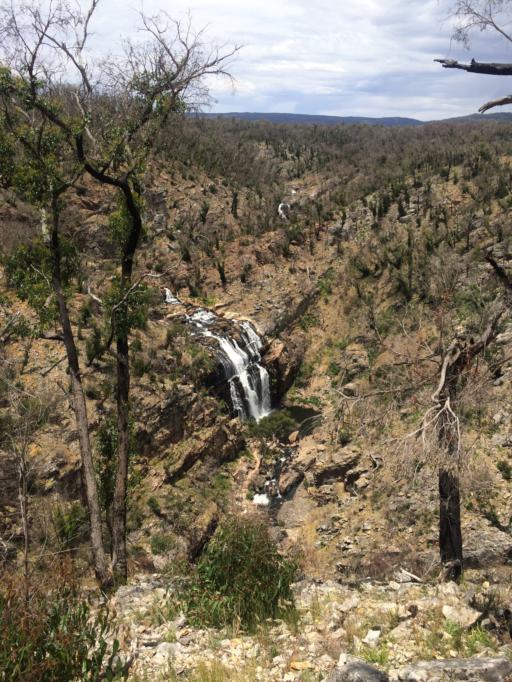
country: AU
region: Victoria
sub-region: Northern Grampians
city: Stawell
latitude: -37.1107
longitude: 142.4070
